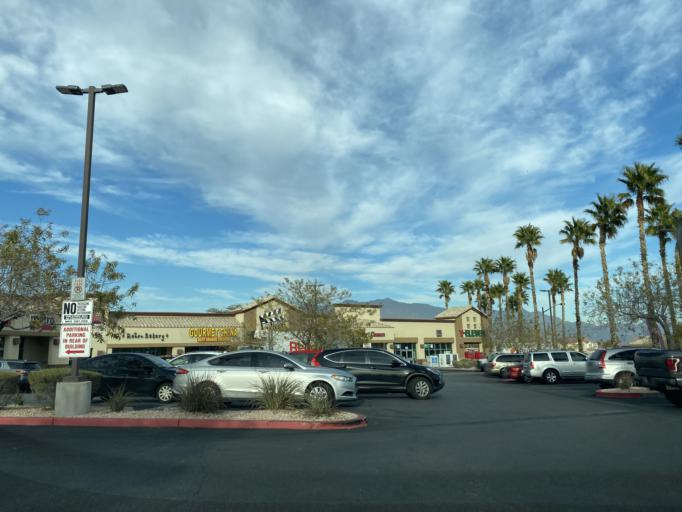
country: US
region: Nevada
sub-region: Clark County
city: Summerlin South
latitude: 36.3022
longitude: -115.2823
